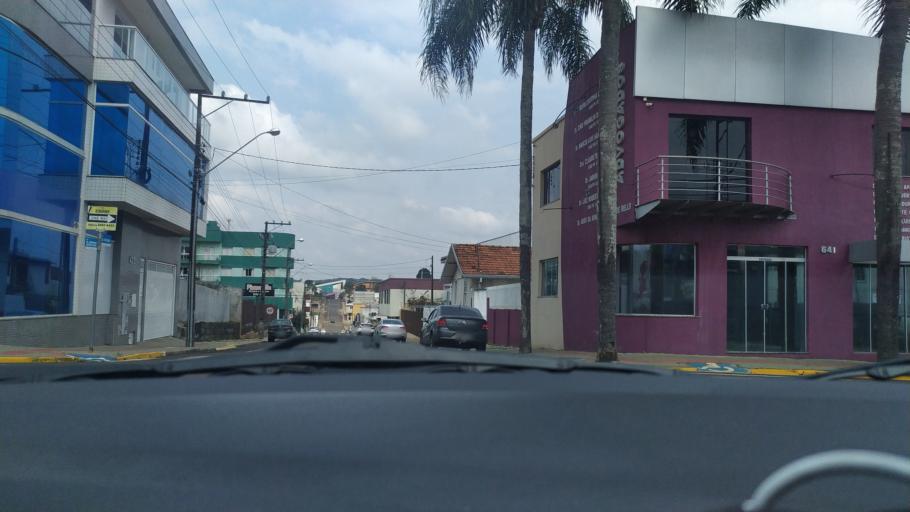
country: BR
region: Parana
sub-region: Palmas
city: Palmas
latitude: -26.4839
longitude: -51.9880
